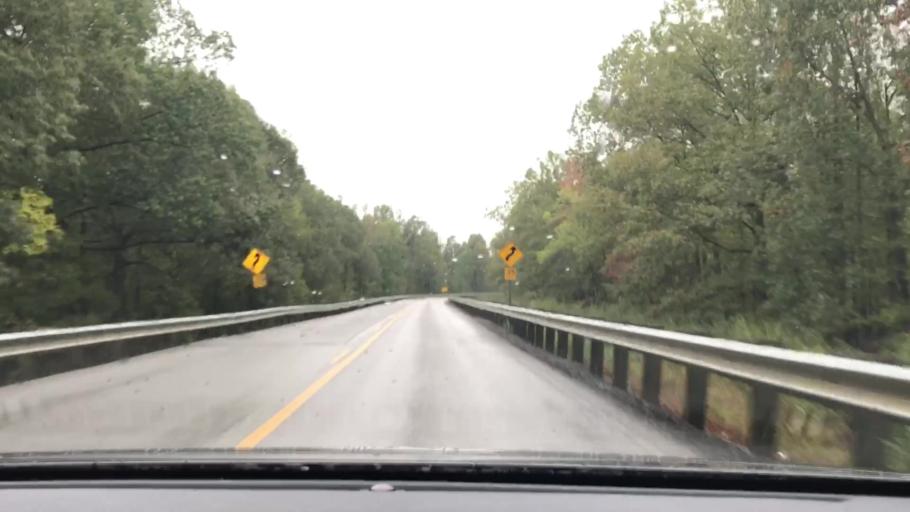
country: US
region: Kentucky
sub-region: McLean County
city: Calhoun
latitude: 37.3948
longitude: -87.2983
